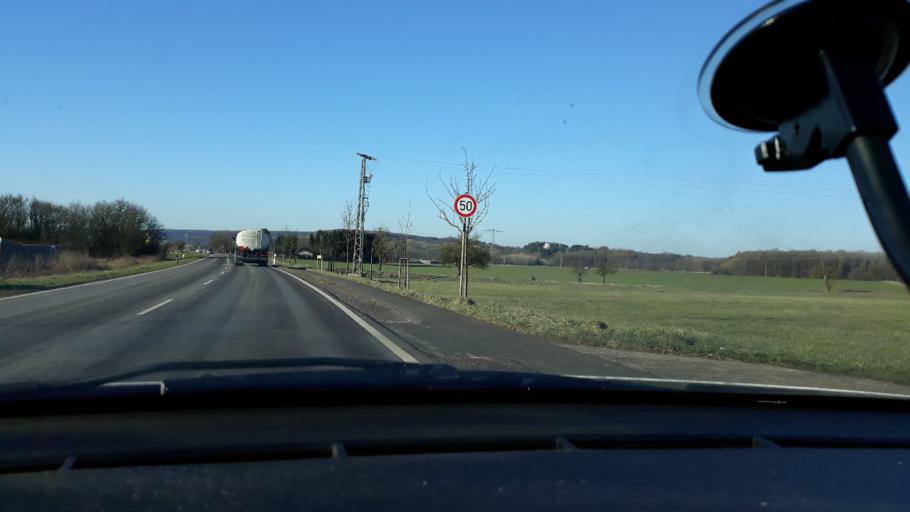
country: DE
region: Saarland
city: Gersheim
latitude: 49.2117
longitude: 7.1803
